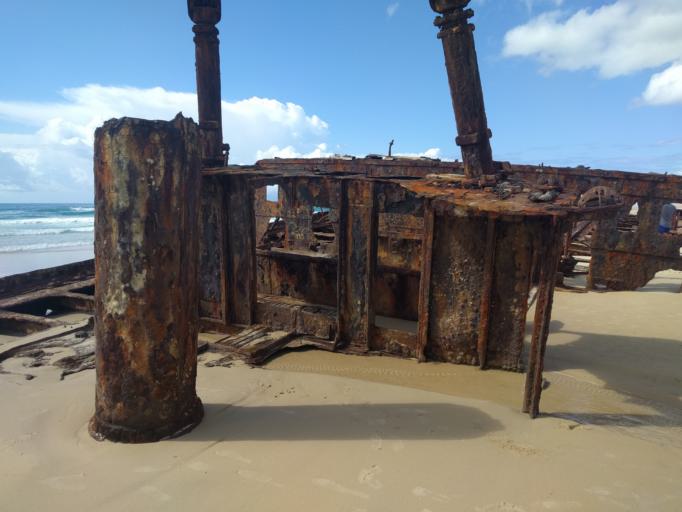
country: AU
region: Queensland
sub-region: Fraser Coast
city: Urangan
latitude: -25.2669
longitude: 153.2384
